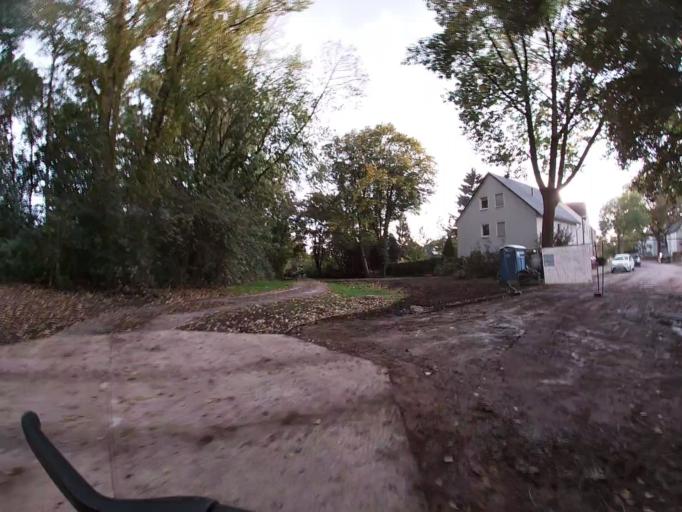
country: DE
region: North Rhine-Westphalia
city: Witten
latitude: 51.4860
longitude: 7.3144
